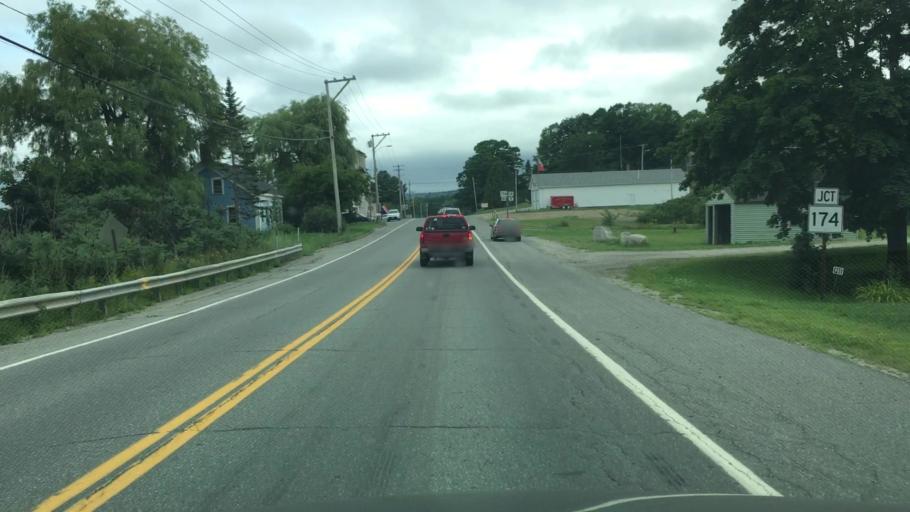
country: US
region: Maine
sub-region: Waldo County
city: Frankfort
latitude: 44.5545
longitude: -68.8644
